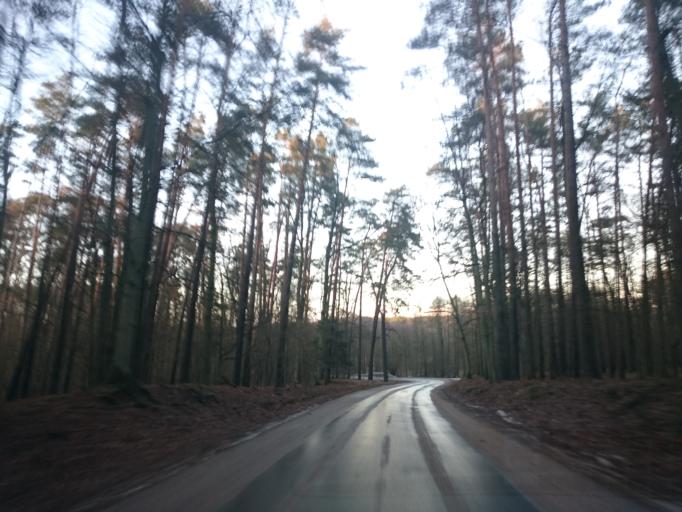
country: PL
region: Kujawsko-Pomorskie
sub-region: Powiat golubsko-dobrzynski
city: Ciechocin
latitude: 53.0868
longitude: 18.9433
